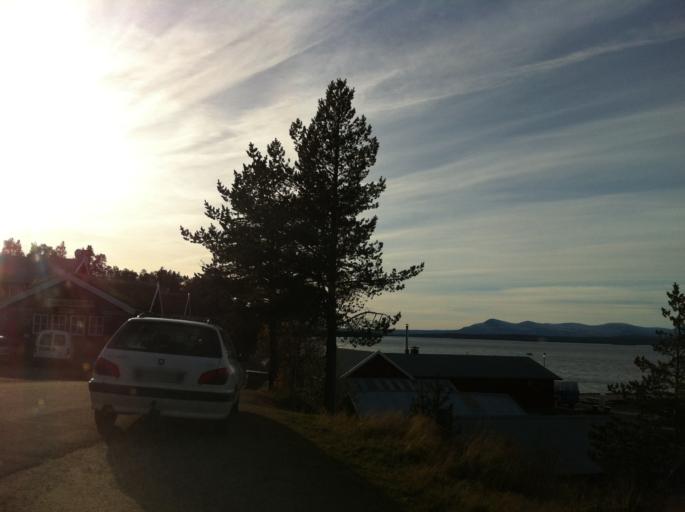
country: NO
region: Hedmark
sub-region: Engerdal
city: Engerdal
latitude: 62.1630
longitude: 11.9446
